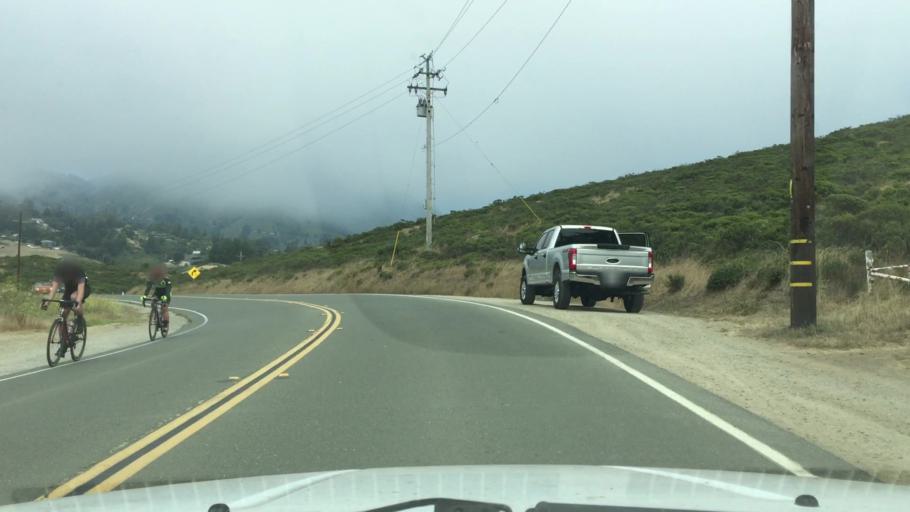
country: US
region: California
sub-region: Marin County
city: Tamalpais Valley
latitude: 37.8893
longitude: -122.5550
